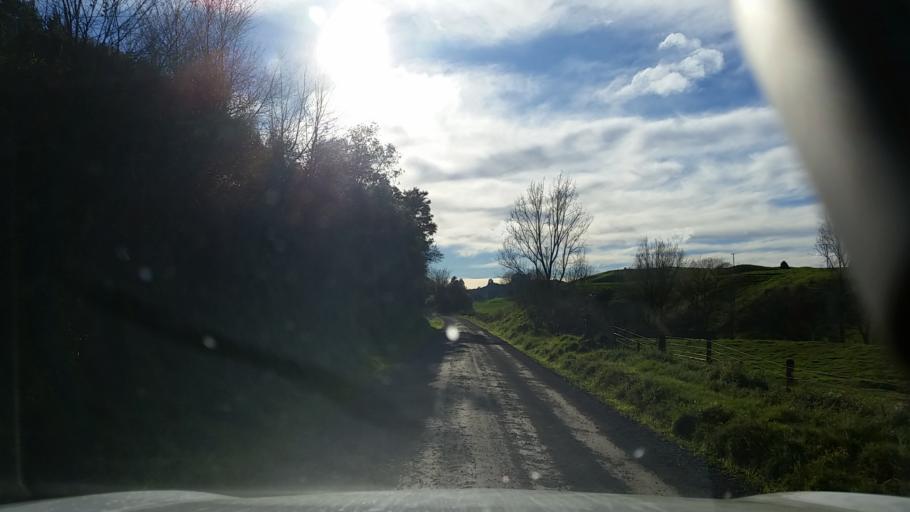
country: NZ
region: Waikato
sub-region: South Waikato District
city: Tokoroa
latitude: -38.3914
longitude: 176.0760
